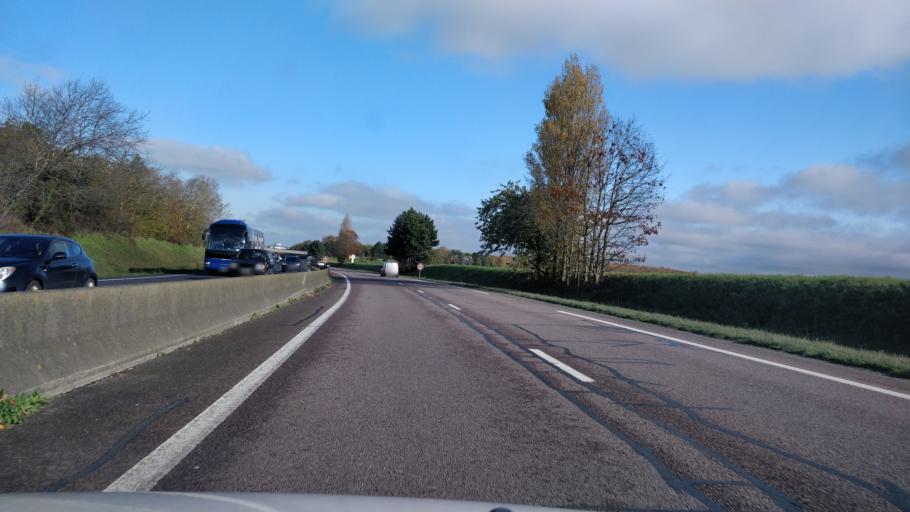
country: FR
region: Lower Normandy
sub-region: Departement du Calvados
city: Fleury-sur-Orne
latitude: 49.1380
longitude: -0.3686
